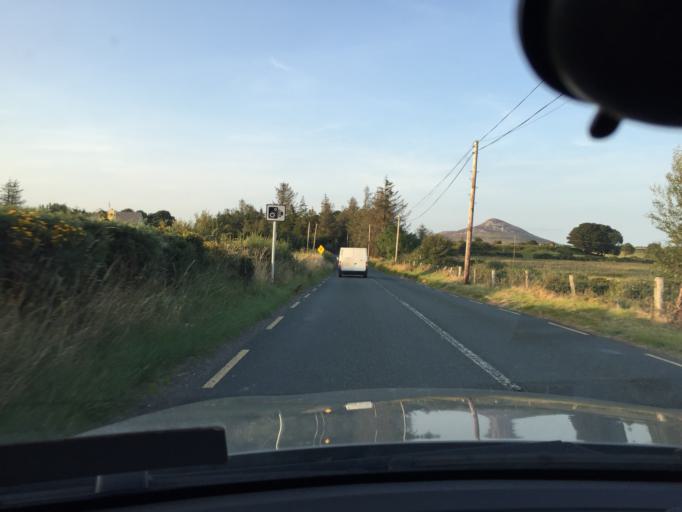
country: IE
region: Leinster
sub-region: Wicklow
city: Kilmacanoge
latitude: 53.1260
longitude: -6.1816
